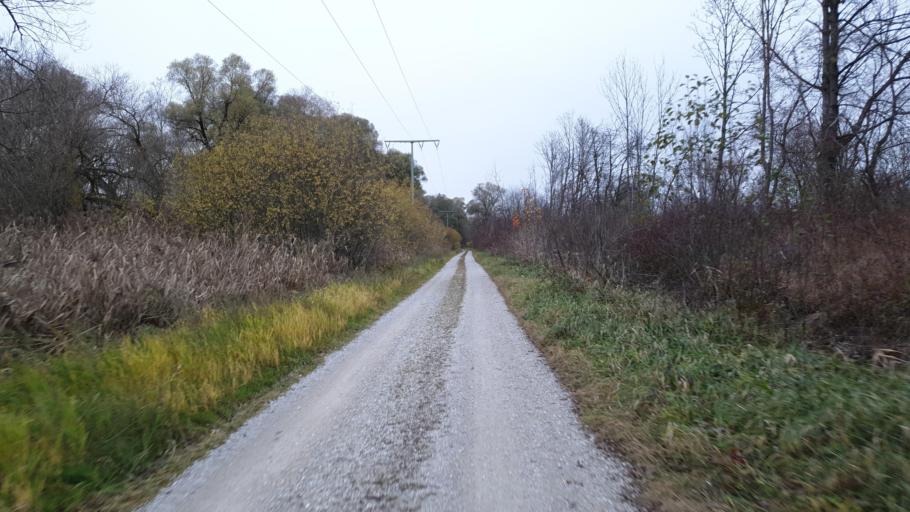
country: DE
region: Bavaria
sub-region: Upper Bavaria
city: Aschheim
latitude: 48.2043
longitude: 11.7101
